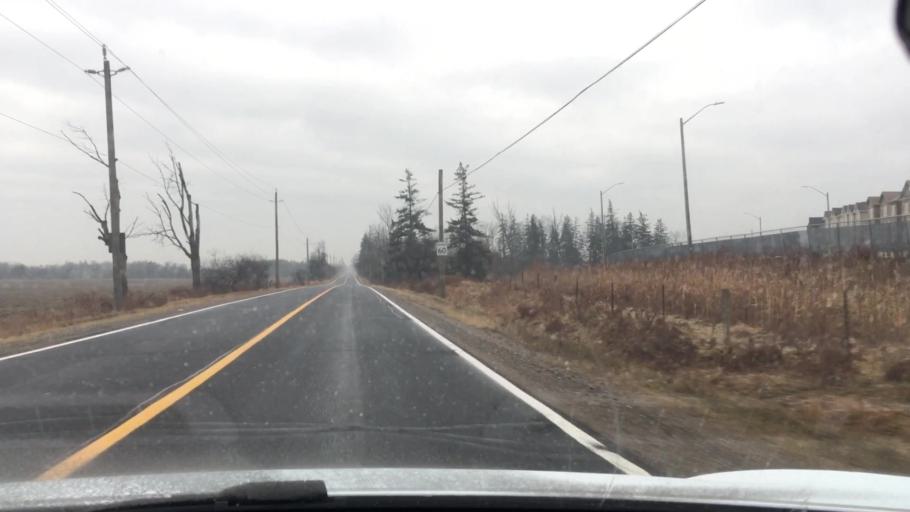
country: CA
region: Ontario
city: Markham
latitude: 43.8922
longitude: -79.2125
